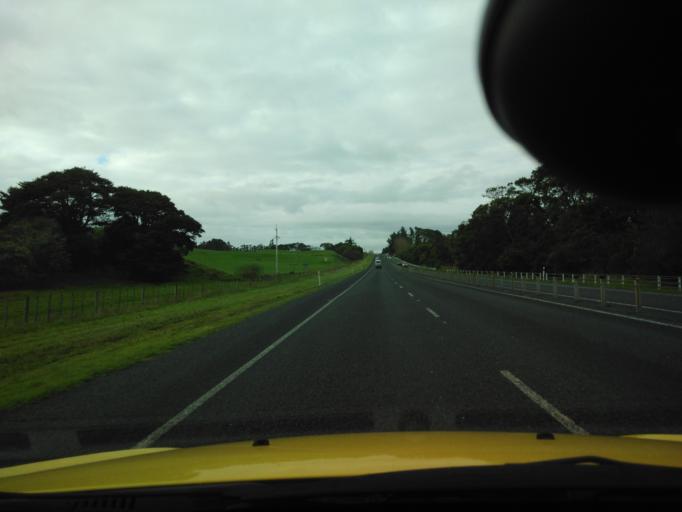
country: NZ
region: Waikato
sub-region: Waikato District
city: Te Kauwhata
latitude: -37.3746
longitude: 175.0956
